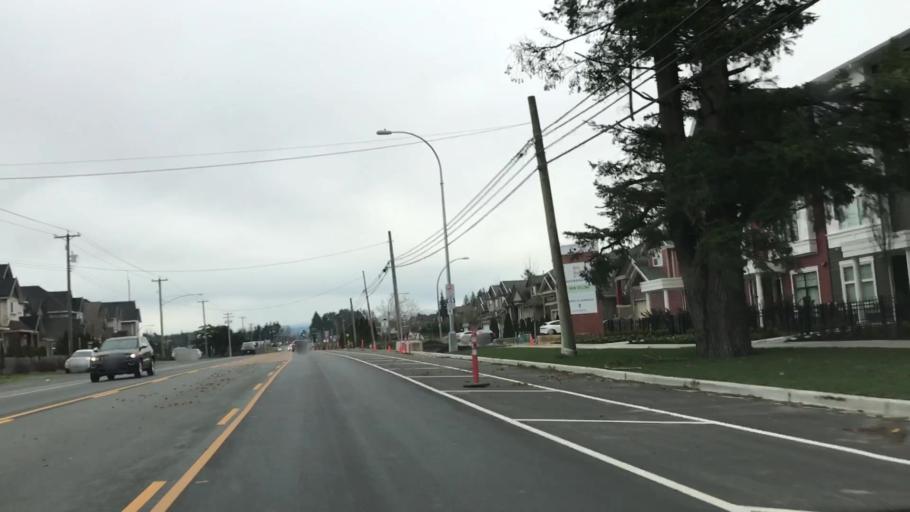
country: CA
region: British Columbia
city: Aldergrove
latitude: 49.0576
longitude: -122.4565
